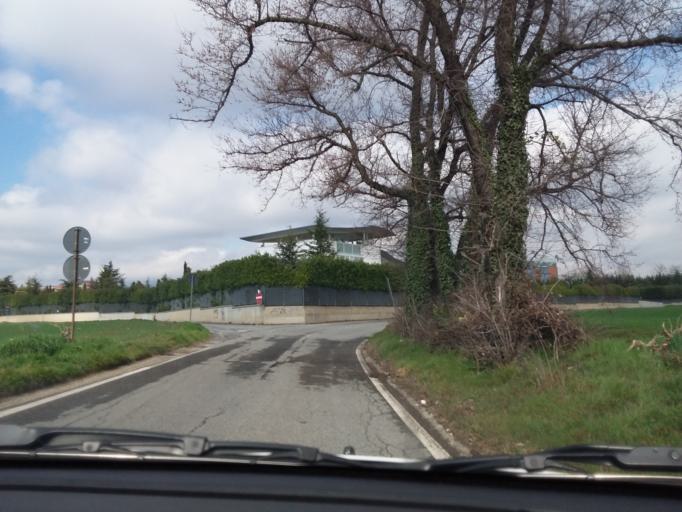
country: IT
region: Piedmont
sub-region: Provincia di Torino
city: Rivoli
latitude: 45.0594
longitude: 7.5269
